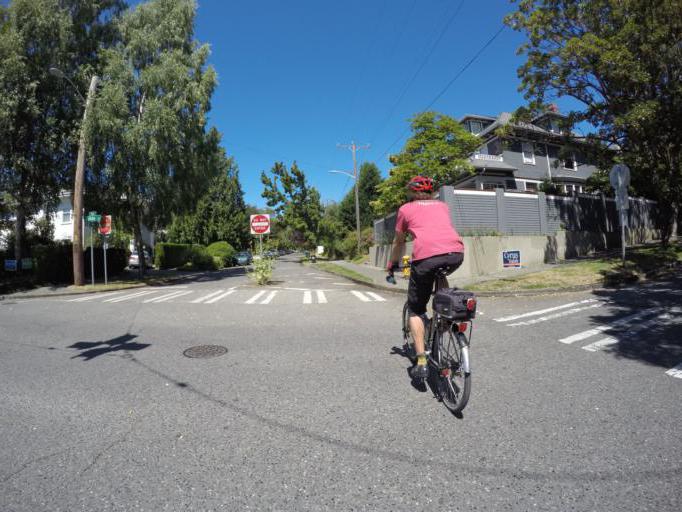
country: US
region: Washington
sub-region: King County
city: Seattle
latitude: 47.6265
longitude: -122.3167
